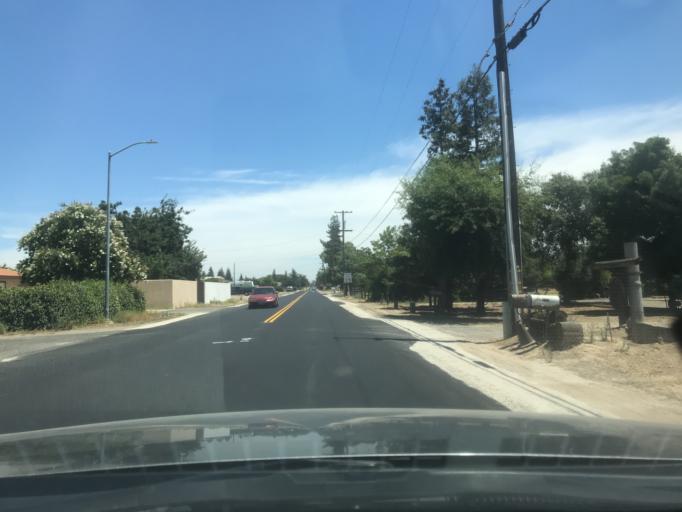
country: US
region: California
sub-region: Merced County
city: Winton
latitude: 37.3713
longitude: -120.6078
